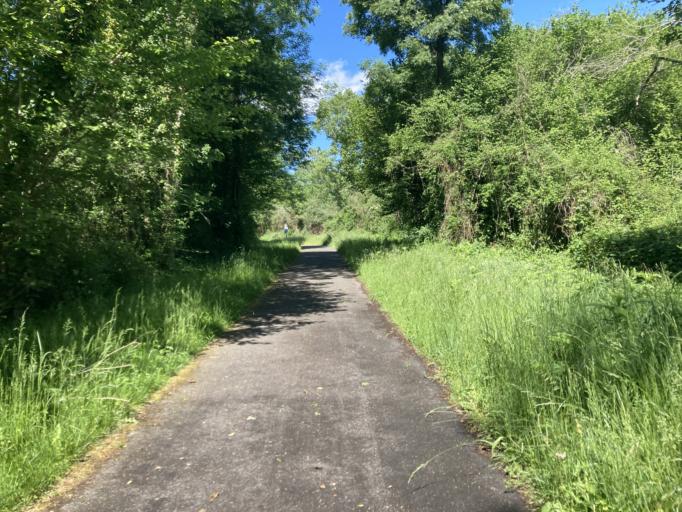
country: FR
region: Aquitaine
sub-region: Departement des Pyrenees-Atlantiques
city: Arbus
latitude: 43.3305
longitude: -0.4811
